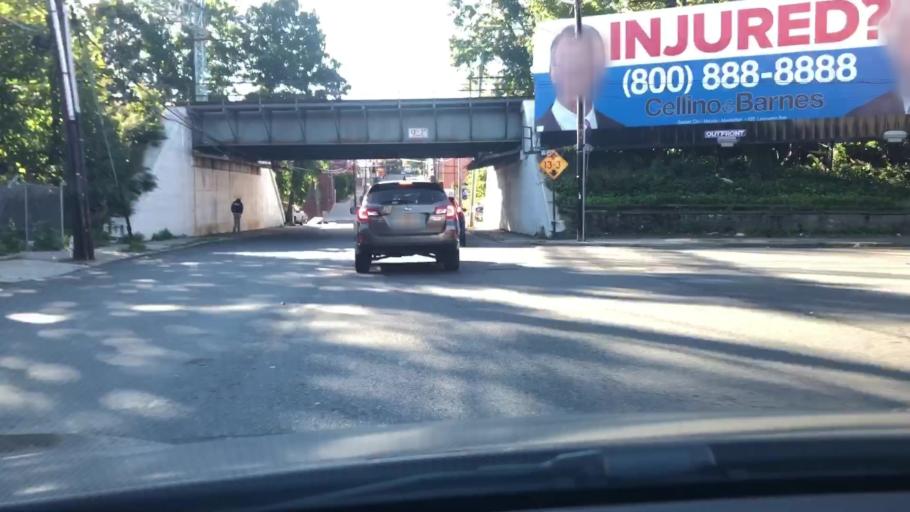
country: US
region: New York
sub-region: Westchester County
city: Mount Vernon
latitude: 40.9124
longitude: -73.8231
